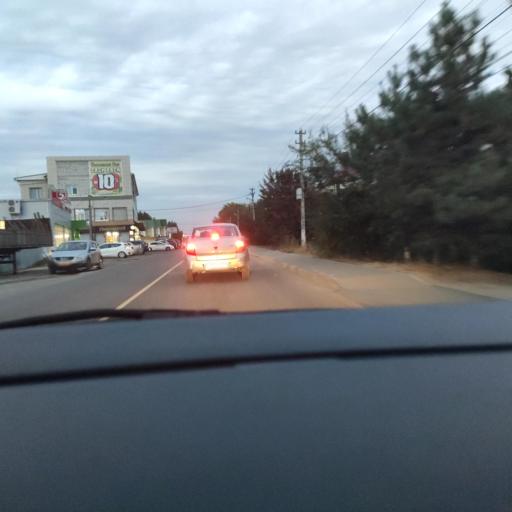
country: RU
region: Voronezj
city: Podgornoye
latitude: 51.7397
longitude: 39.1640
